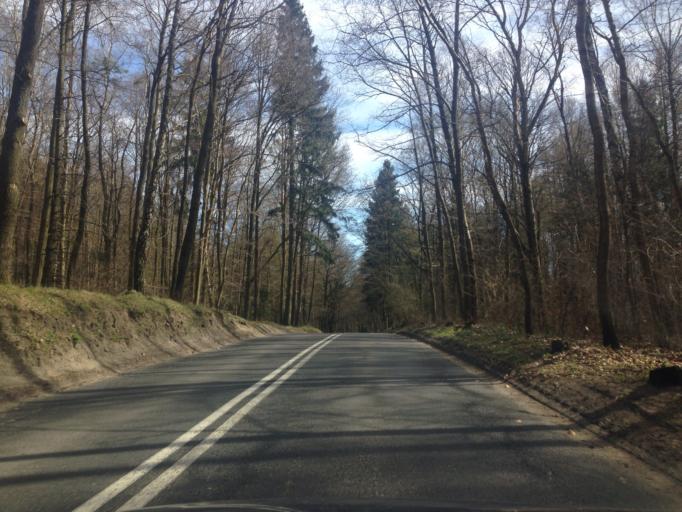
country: PL
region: Pomeranian Voivodeship
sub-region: Gdynia
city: Wielki Kack
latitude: 54.4806
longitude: 18.4468
